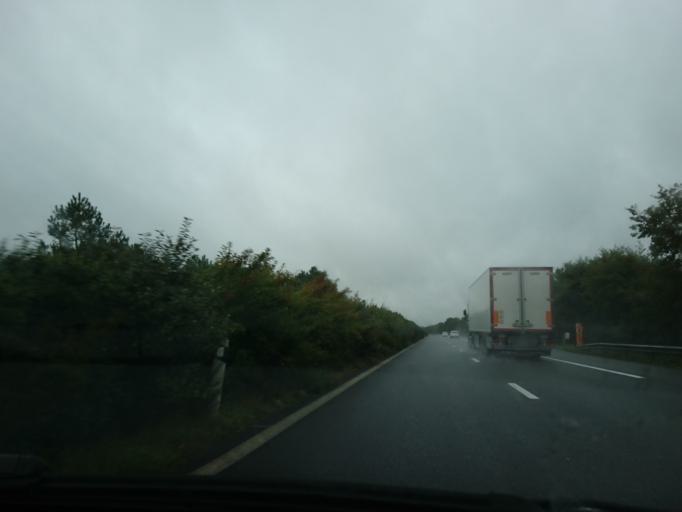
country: FR
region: Pays de la Loire
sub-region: Departement de la Loire-Atlantique
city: La Chapelle-des-Marais
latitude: 47.4916
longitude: -2.2379
